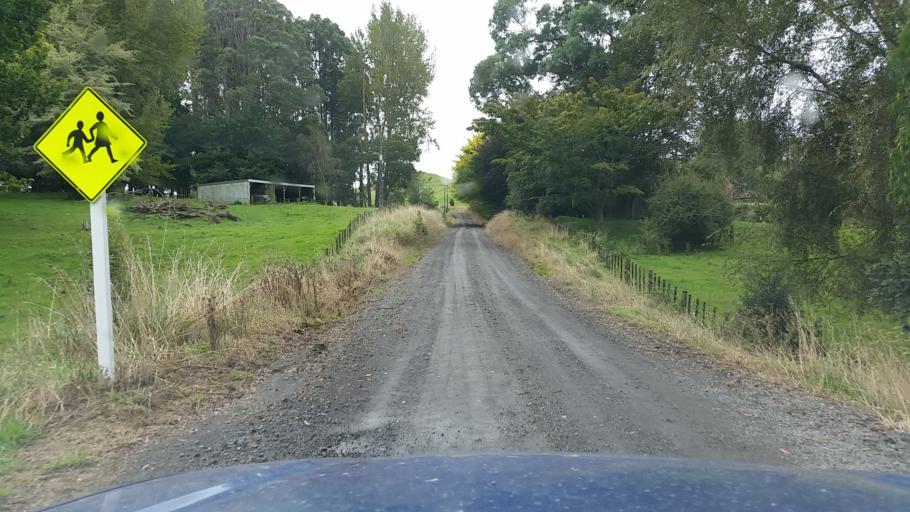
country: NZ
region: Taranaki
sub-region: South Taranaki District
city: Eltham
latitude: -39.3566
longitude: 174.4338
